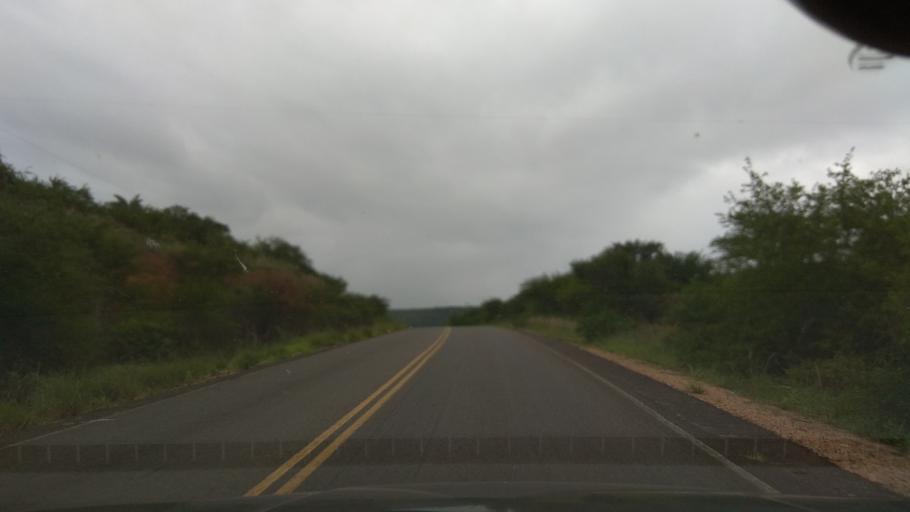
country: BR
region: Bahia
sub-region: Santa Ines
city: Santa Ines
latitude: -13.2702
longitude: -39.8001
